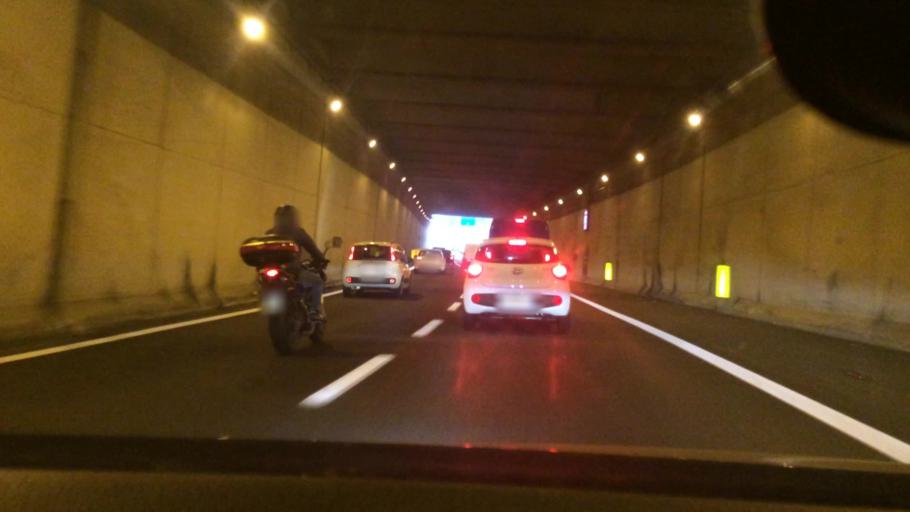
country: IT
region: Lombardy
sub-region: Citta metropolitana di Milano
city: Pero
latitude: 45.5147
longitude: 9.0784
